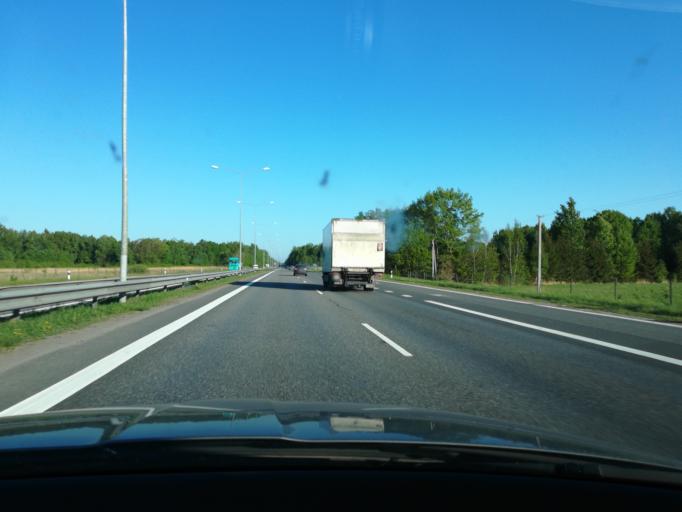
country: LT
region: Kauno apskritis
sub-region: Kauno rajonas
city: Karmelava
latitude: 54.8971
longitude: 24.1464
